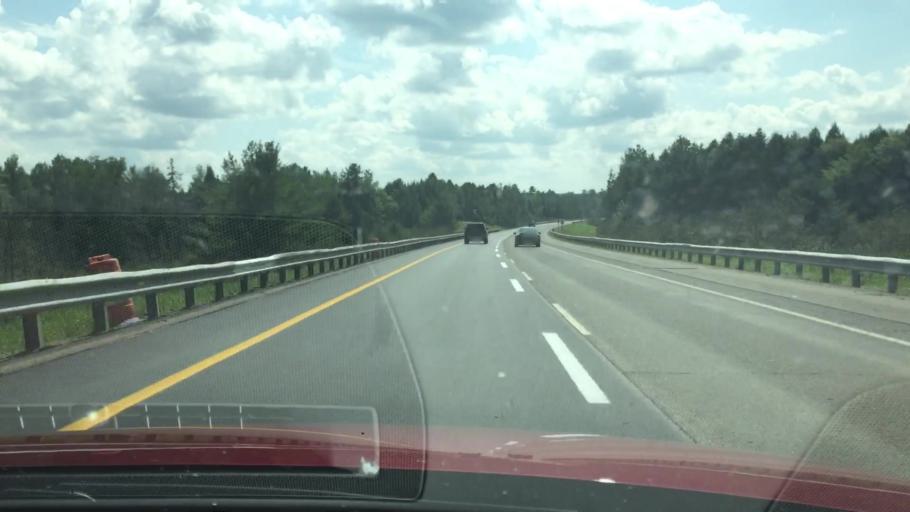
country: US
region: Maine
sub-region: Penobscot County
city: Medway
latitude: 45.6435
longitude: -68.4996
